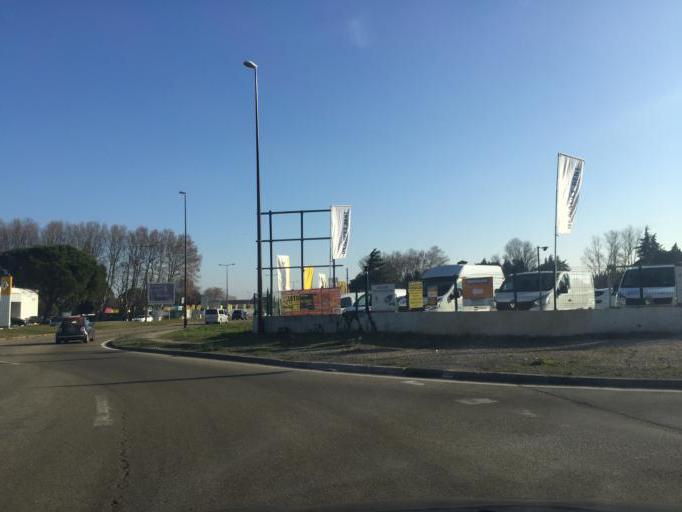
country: FR
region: Provence-Alpes-Cote d'Azur
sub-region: Departement du Vaucluse
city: Montfavet
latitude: 43.9265
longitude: 4.8450
